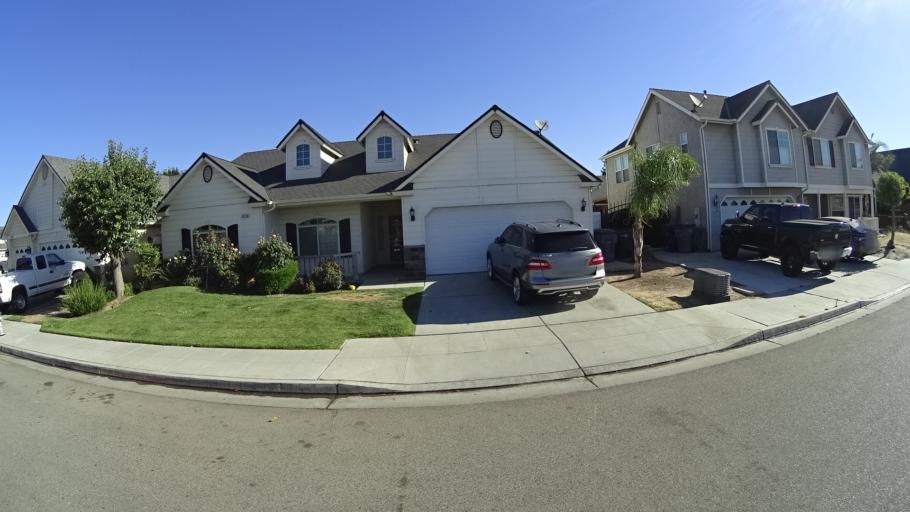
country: US
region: California
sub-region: Fresno County
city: West Park
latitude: 36.7810
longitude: -119.8651
